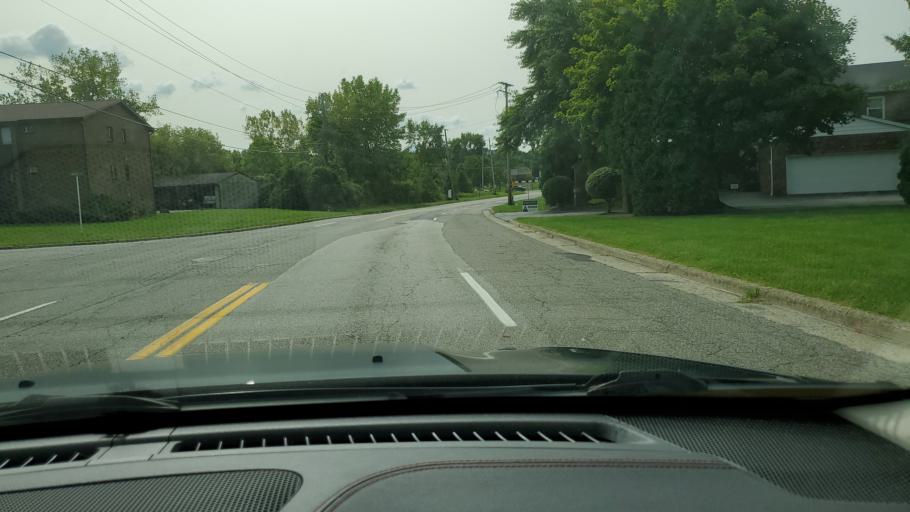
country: US
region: Ohio
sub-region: Mahoning County
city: Boardman
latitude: 40.9898
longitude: -80.6696
